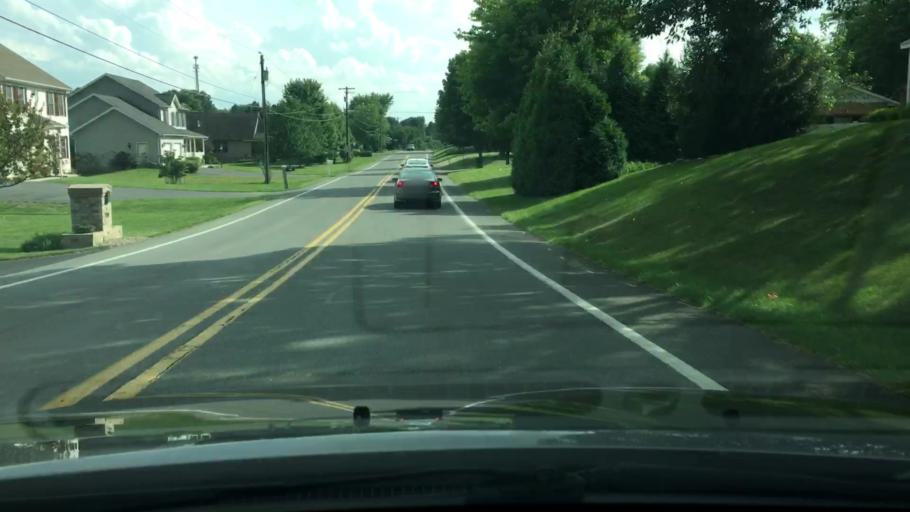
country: US
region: Pennsylvania
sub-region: Franklin County
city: Guilford
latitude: 39.9270
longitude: -77.5910
